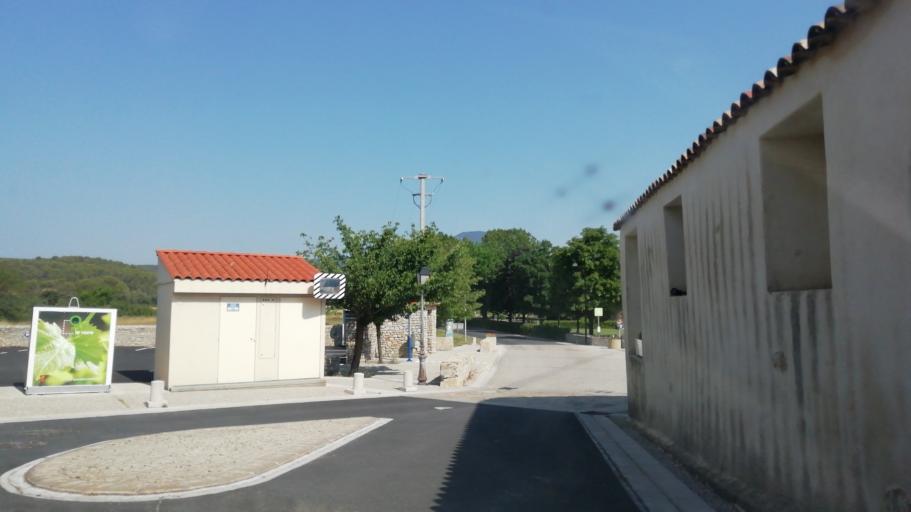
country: FR
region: Languedoc-Roussillon
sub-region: Departement de l'Herault
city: Saint-Mathieu-de-Treviers
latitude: 43.7400
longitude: 3.8520
